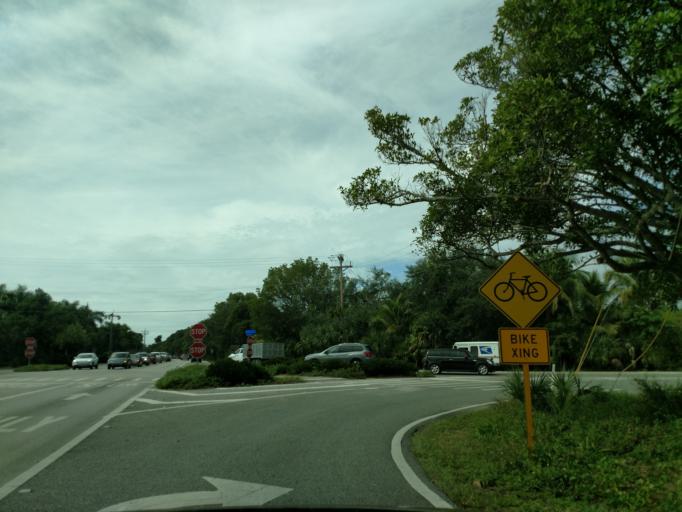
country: US
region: Florida
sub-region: Lee County
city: Sanibel
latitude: 26.4475
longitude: -82.0380
